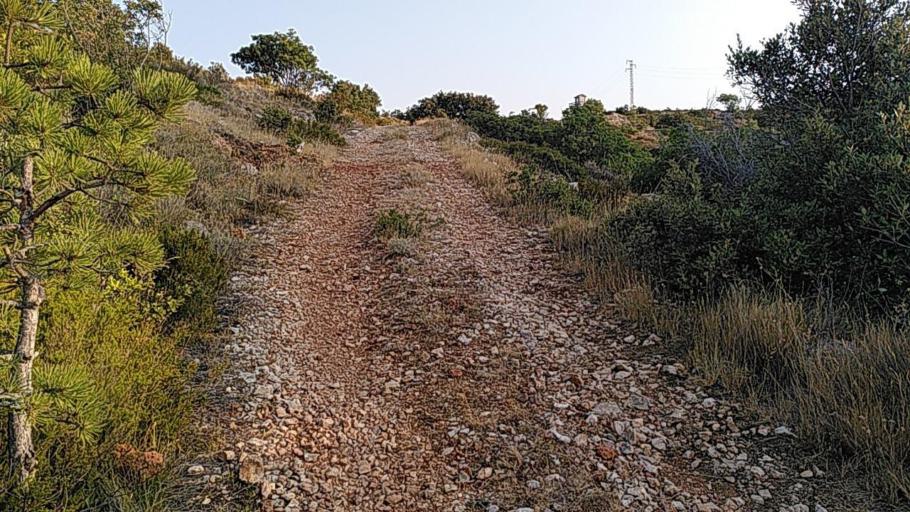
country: HR
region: Splitsko-Dalmatinska
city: Jelsa
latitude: 43.1341
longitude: 16.6802
